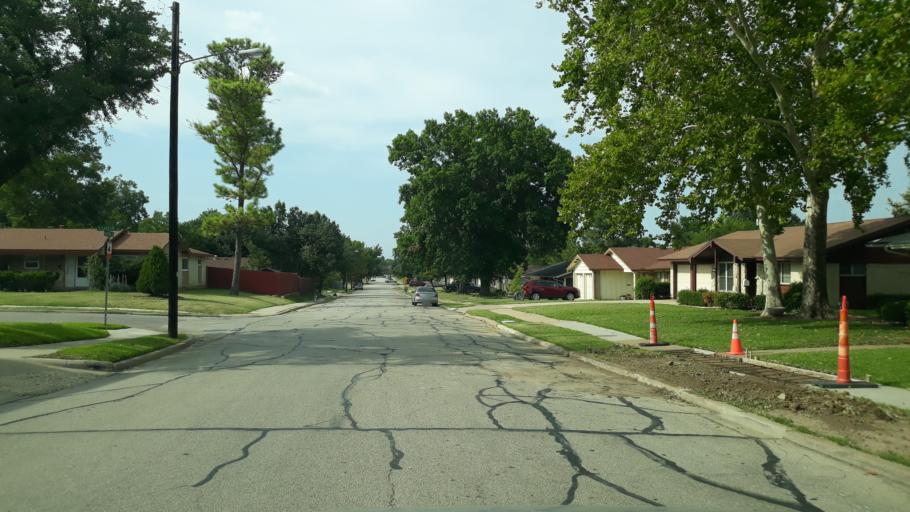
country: US
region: Texas
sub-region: Dallas County
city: Irving
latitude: 32.8442
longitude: -96.9887
